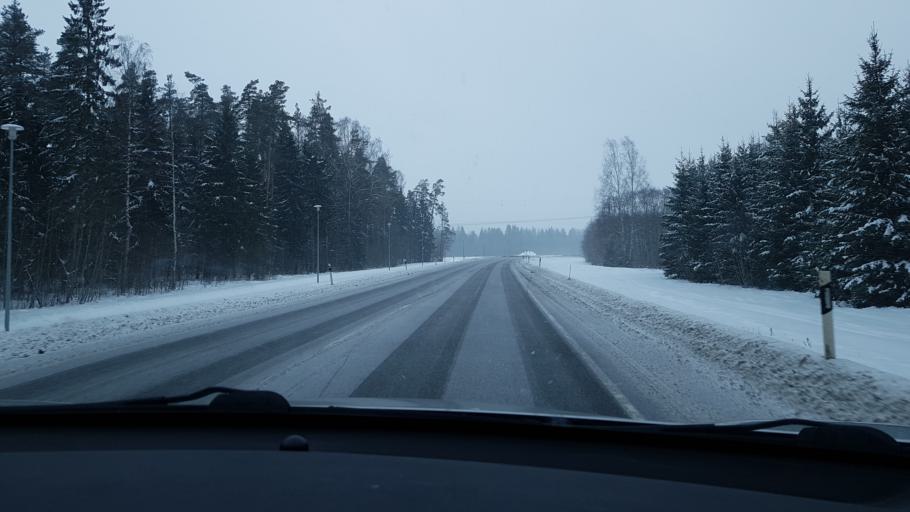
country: EE
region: Jaervamaa
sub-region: Paide linn
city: Paide
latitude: 58.8698
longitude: 25.4947
